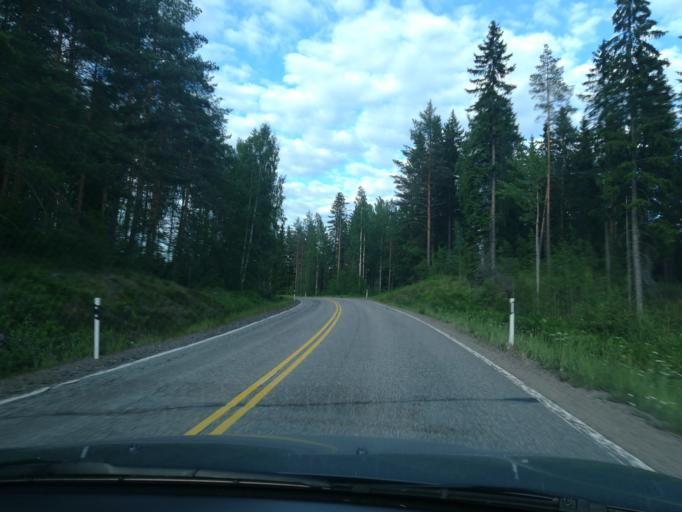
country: FI
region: Southern Savonia
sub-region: Mikkeli
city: Puumala
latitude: 61.5159
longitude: 27.9067
